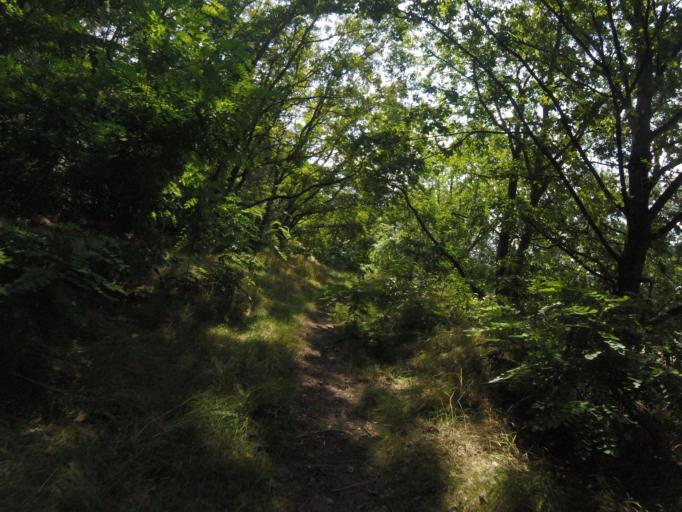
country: DE
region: Brandenburg
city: Wildau
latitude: 52.3243
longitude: 13.6083
